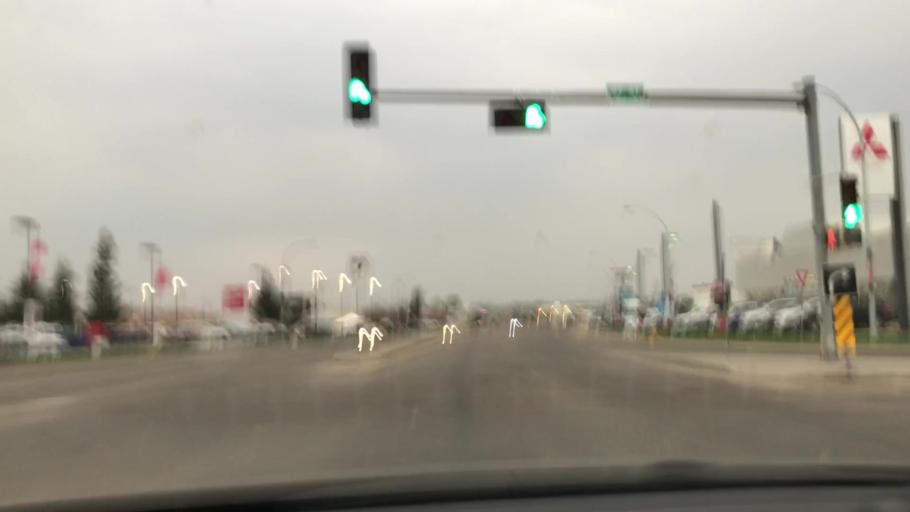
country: CA
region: Alberta
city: Edmonton
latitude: 53.4672
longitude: -113.4797
